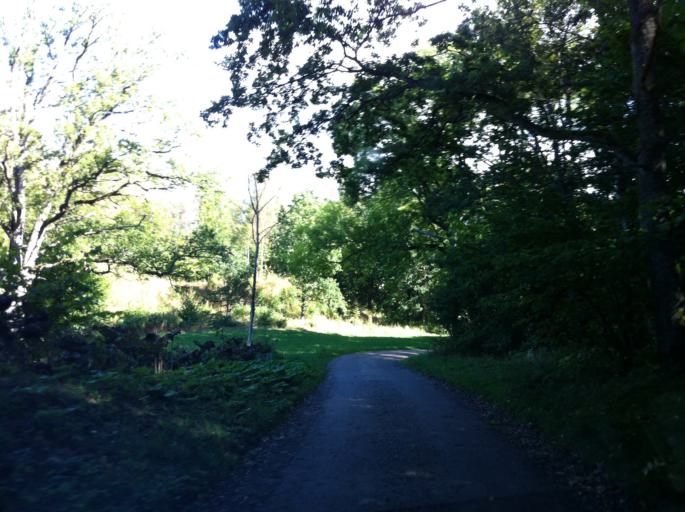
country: SE
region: Skane
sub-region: Kristianstads Kommun
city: Degeberga
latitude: 55.7369
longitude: 13.9354
